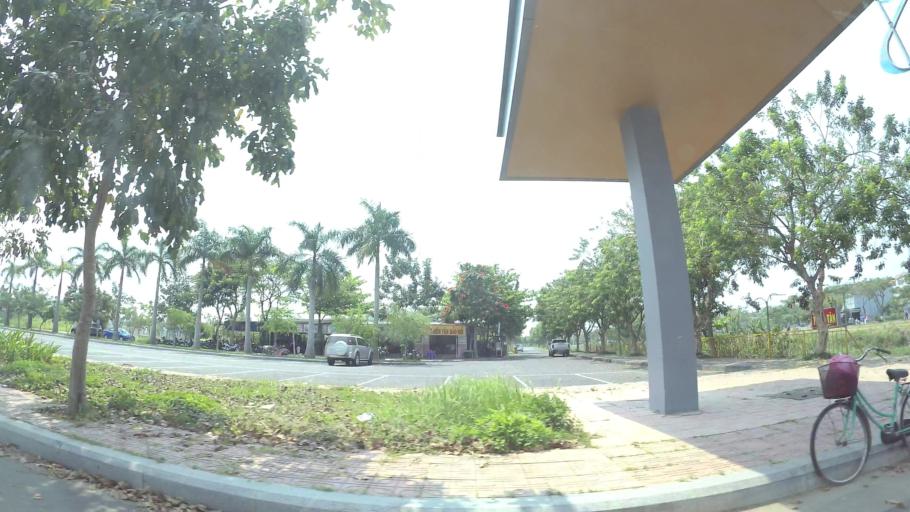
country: VN
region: Da Nang
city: Cam Le
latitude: 16.0147
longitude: 108.2105
